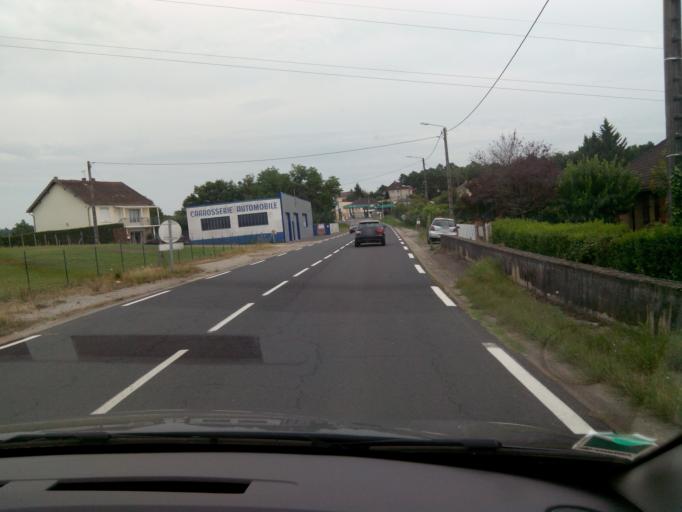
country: FR
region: Limousin
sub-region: Departement de la Correze
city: Cosnac
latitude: 45.1178
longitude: 1.5583
